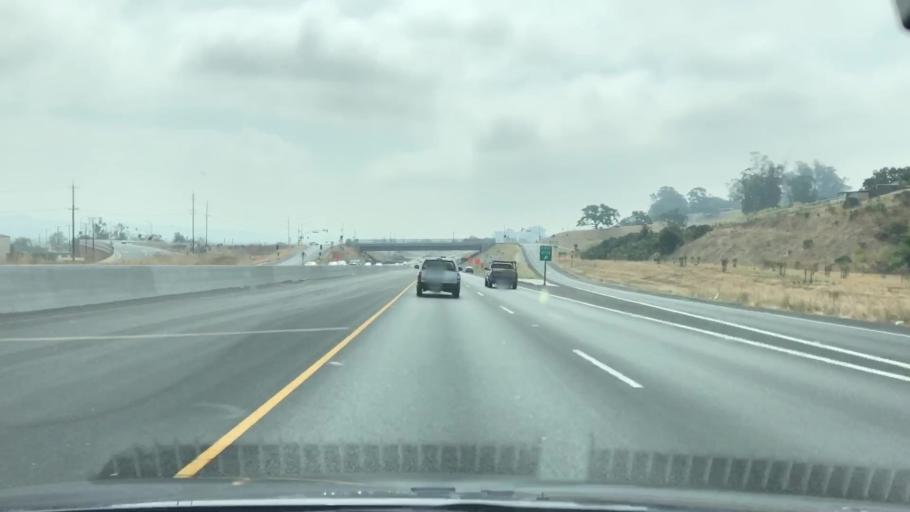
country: US
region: California
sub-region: Sonoma County
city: Petaluma
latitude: 38.2230
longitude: -122.6109
